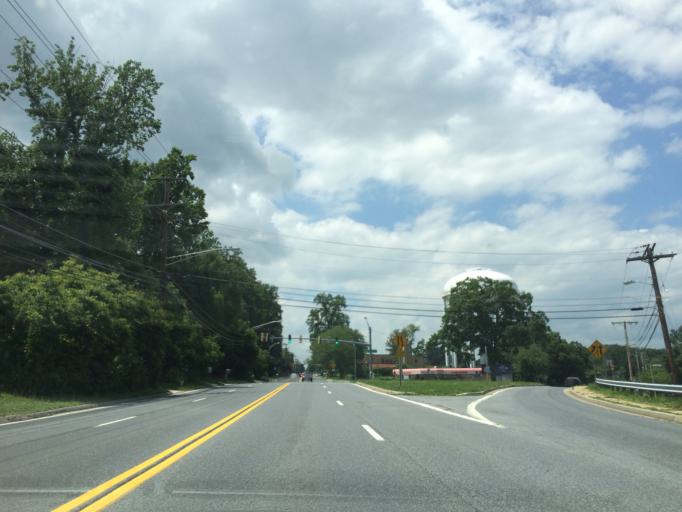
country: US
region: Maryland
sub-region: Baltimore County
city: Randallstown
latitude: 39.3824
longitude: -76.8254
